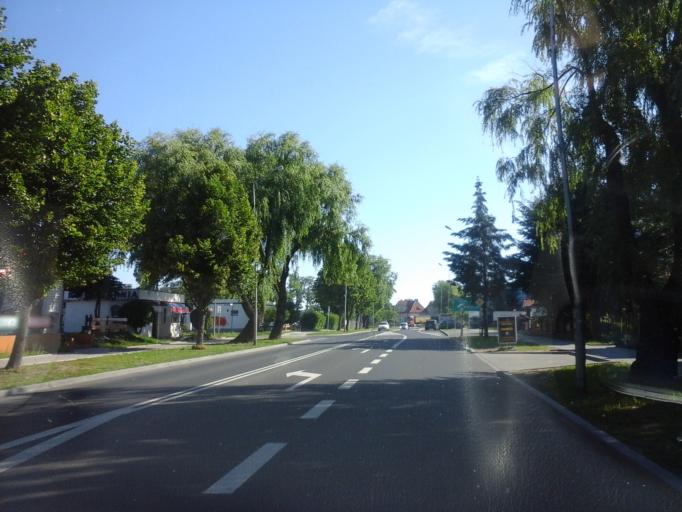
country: PL
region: West Pomeranian Voivodeship
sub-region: Powiat drawski
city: Drawsko Pomorskie
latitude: 53.5358
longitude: 15.8107
